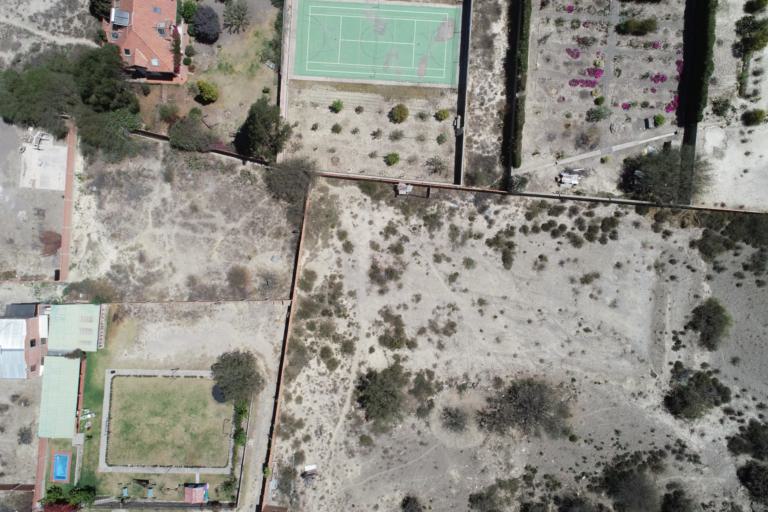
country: BO
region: La Paz
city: La Paz
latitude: -16.6275
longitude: -68.0547
